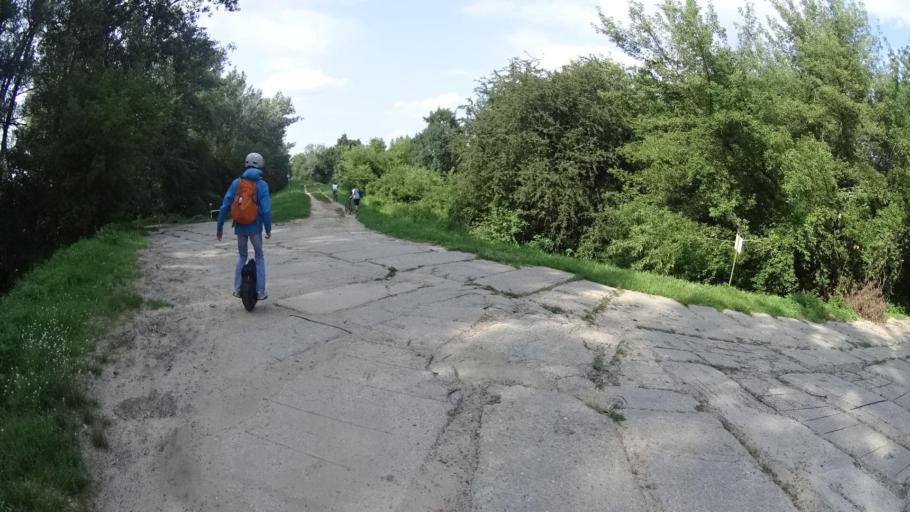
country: PL
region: Masovian Voivodeship
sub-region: Powiat legionowski
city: Jablonna
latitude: 52.3608
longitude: 20.9193
